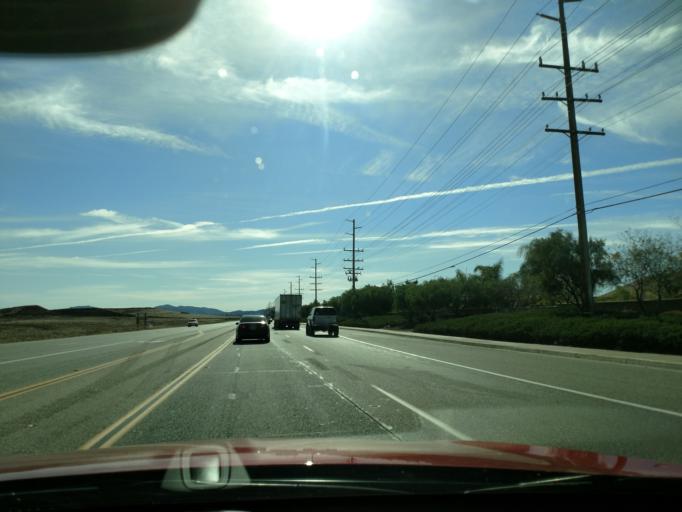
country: US
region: California
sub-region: Riverside County
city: Murrieta Hot Springs
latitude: 33.5754
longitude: -117.1349
